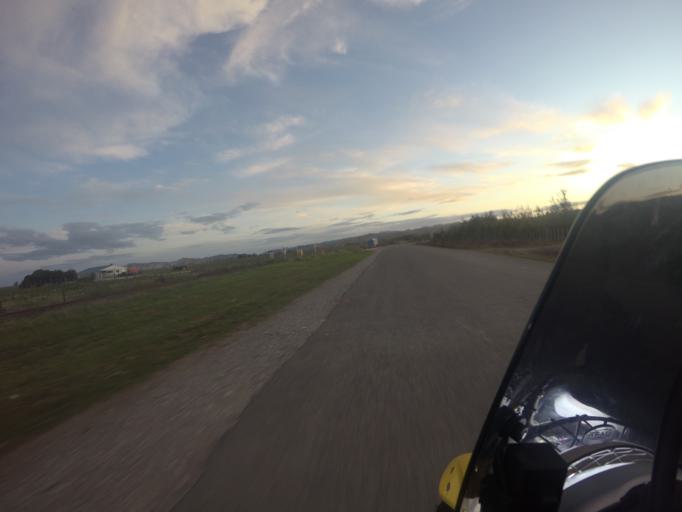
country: NZ
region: Gisborne
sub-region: Gisborne District
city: Gisborne
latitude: -38.6984
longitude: 177.9356
